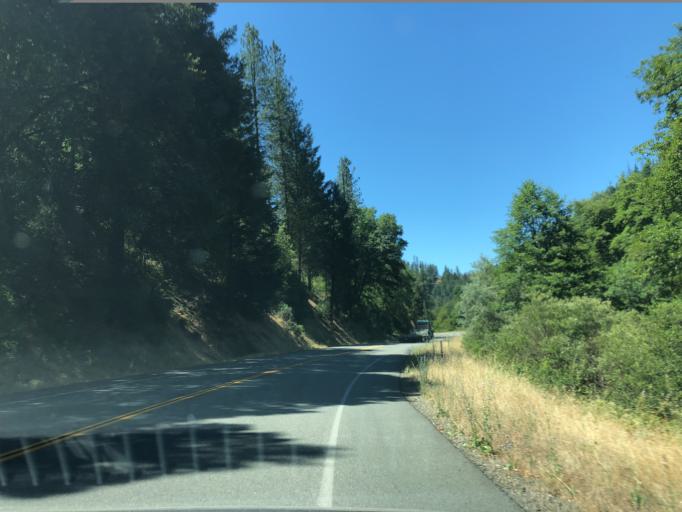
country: US
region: California
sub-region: Trinity County
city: Weaverville
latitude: 40.6865
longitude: -122.9327
